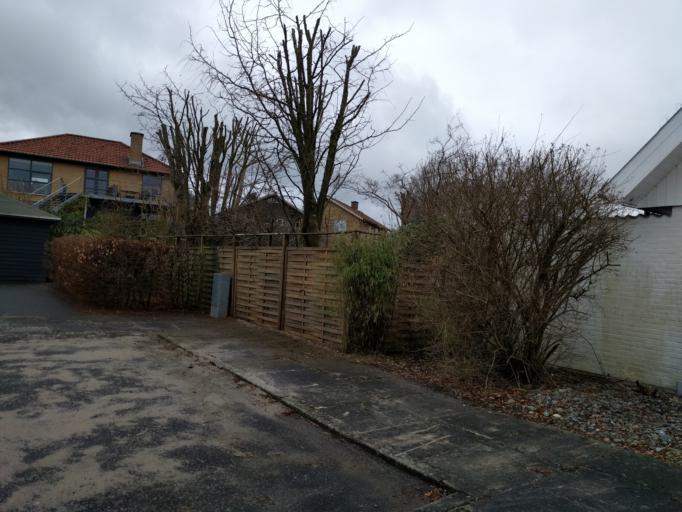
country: DK
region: Central Jutland
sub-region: Silkeborg Kommune
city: Silkeborg
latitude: 56.1816
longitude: 9.5225
